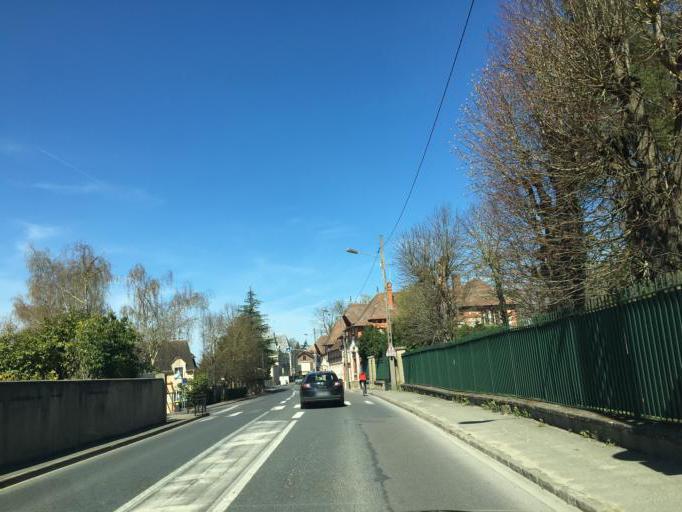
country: FR
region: Ile-de-France
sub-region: Departement de l'Essonne
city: Ris-Orangis
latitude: 48.6665
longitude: 2.4179
